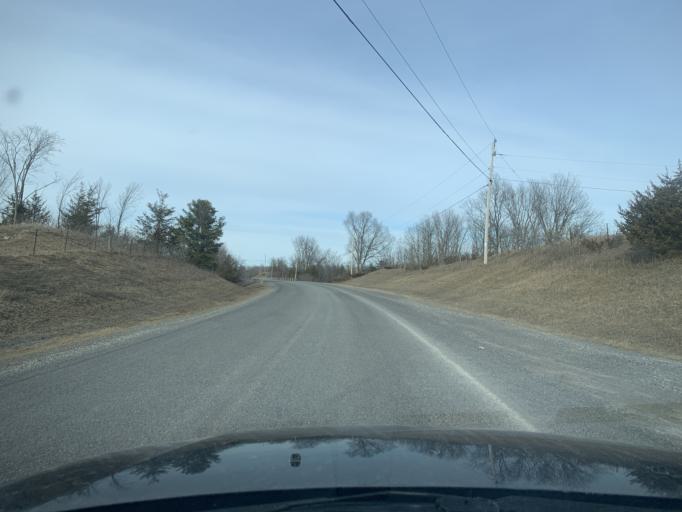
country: CA
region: Ontario
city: Greater Napanee
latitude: 44.4612
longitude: -77.0575
